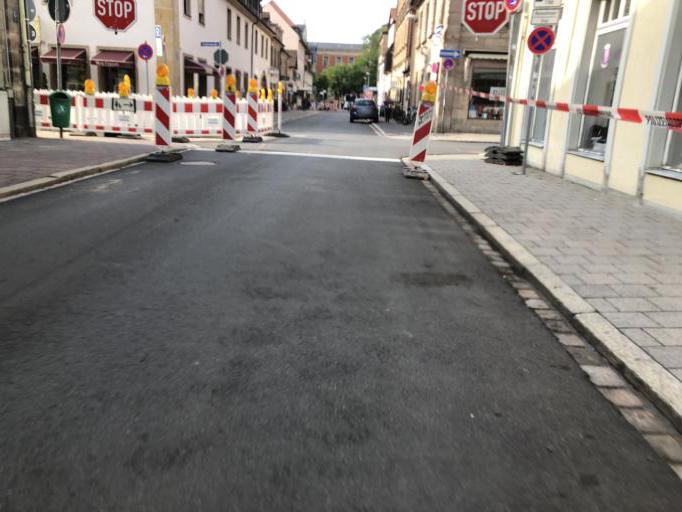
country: DE
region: Bavaria
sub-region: Regierungsbezirk Mittelfranken
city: Erlangen
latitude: 49.5956
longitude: 11.0076
